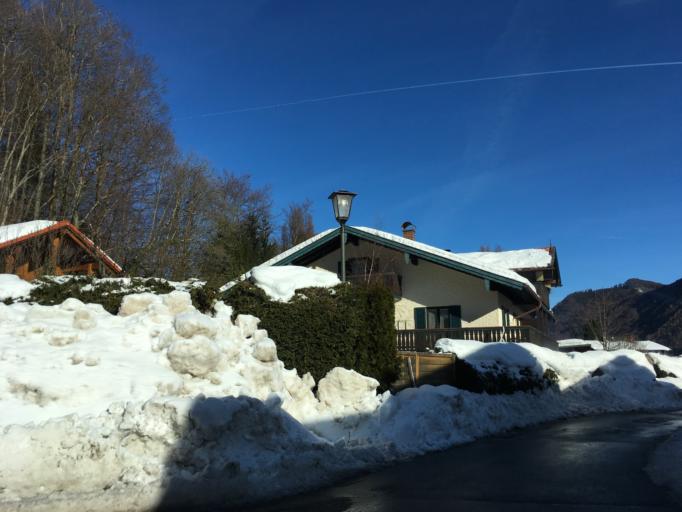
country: DE
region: Bavaria
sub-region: Upper Bavaria
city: Aschau im Chiemgau
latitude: 47.7720
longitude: 12.3170
